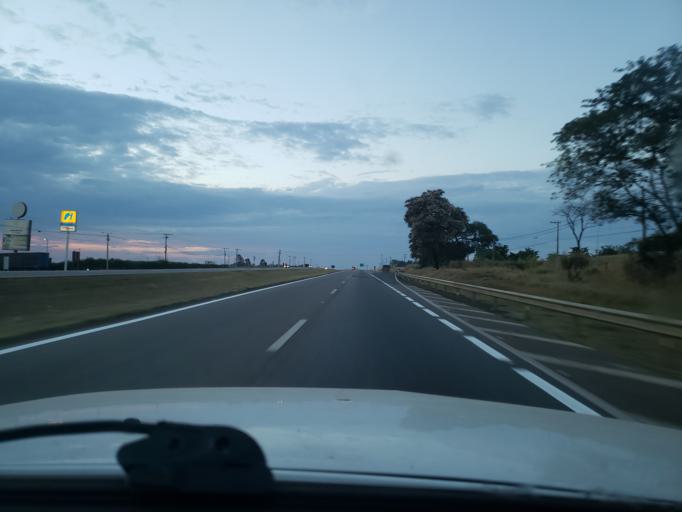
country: BR
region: Sao Paulo
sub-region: Mogi-Mirim
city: Mogi Mirim
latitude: -22.4804
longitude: -46.9812
